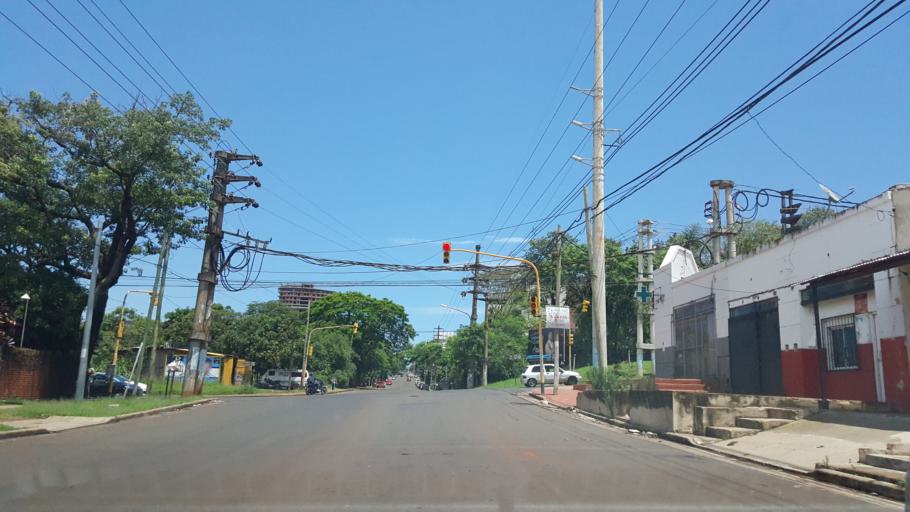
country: AR
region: Misiones
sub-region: Departamento de Capital
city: Posadas
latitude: -27.3597
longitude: -55.9042
